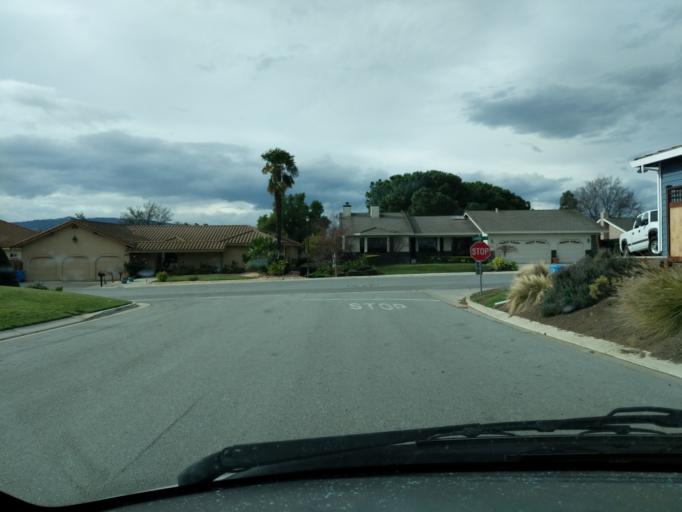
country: US
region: California
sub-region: San Benito County
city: Ridgemark
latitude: 36.8093
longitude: -121.3554
